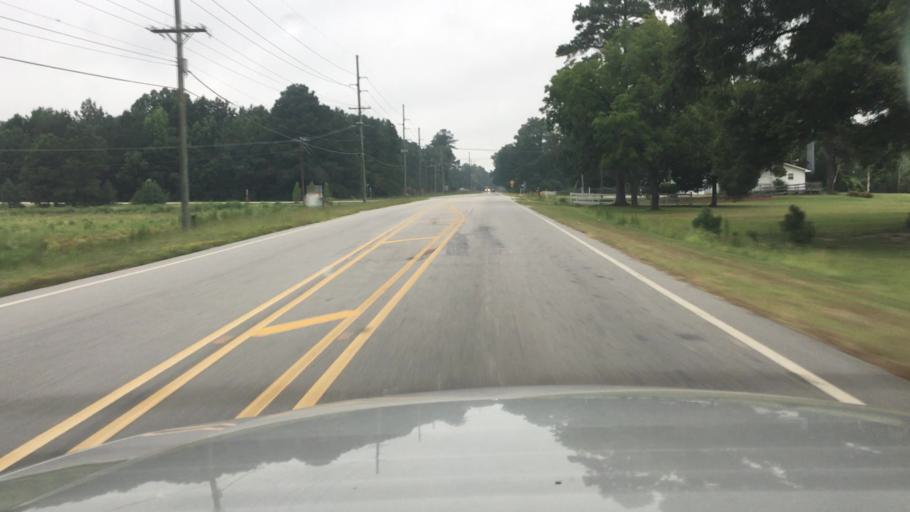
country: US
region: North Carolina
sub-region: Cumberland County
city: Fayetteville
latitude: 35.0091
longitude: -78.8634
